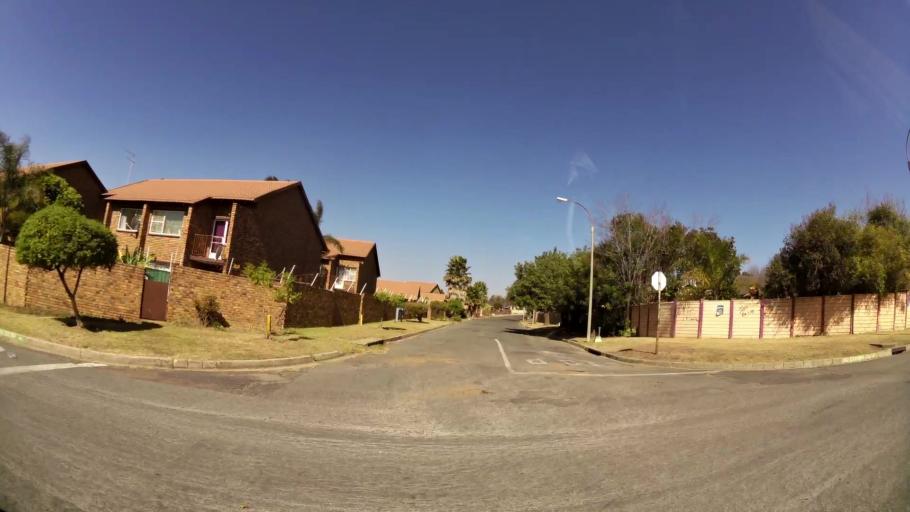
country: ZA
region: Gauteng
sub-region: City of Johannesburg Metropolitan Municipality
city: Modderfontein
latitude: -26.0543
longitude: 28.2101
